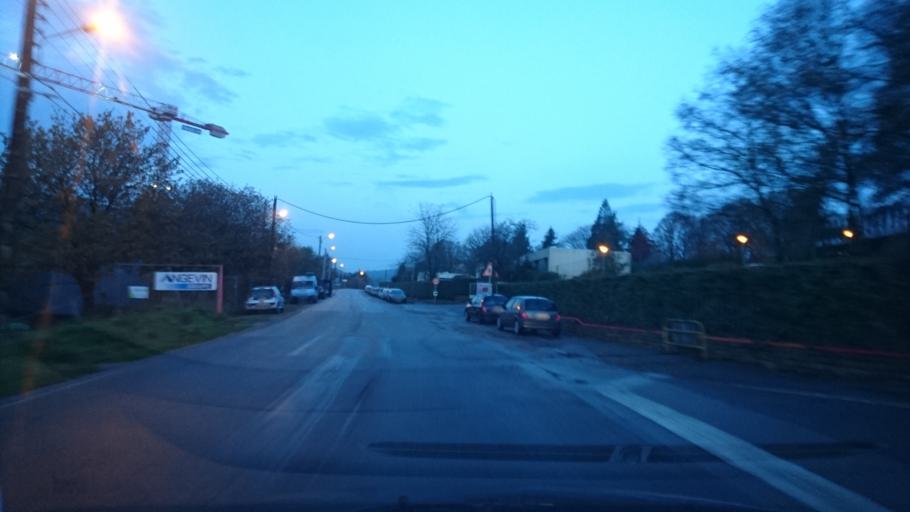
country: FR
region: Brittany
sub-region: Departement du Finistere
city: Chateaulin
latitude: 48.1911
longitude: -4.0858
